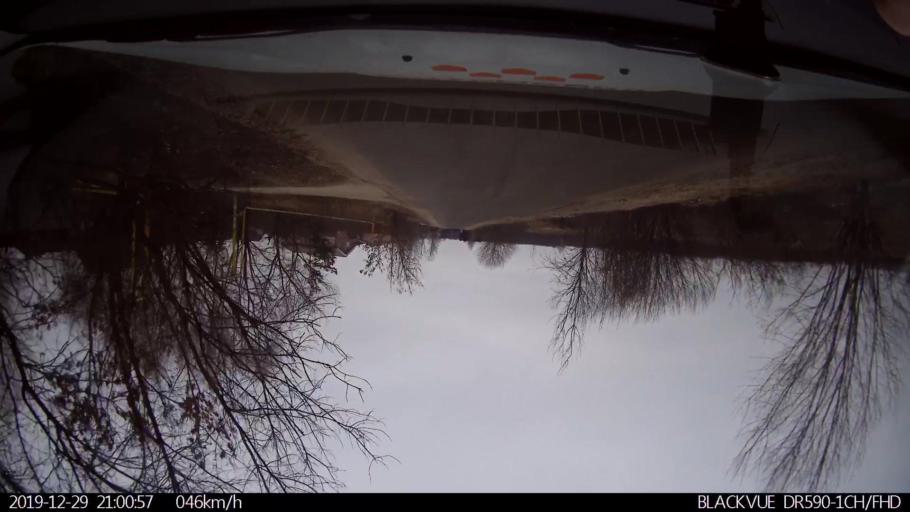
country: RU
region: Nizjnij Novgorod
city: Afonino
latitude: 56.1854
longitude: 43.9900
